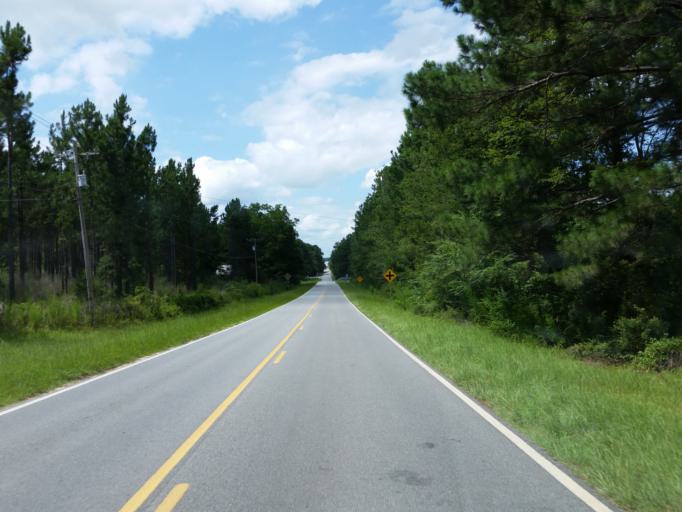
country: US
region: Georgia
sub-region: Tift County
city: Unionville
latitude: 31.4012
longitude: -83.5180
